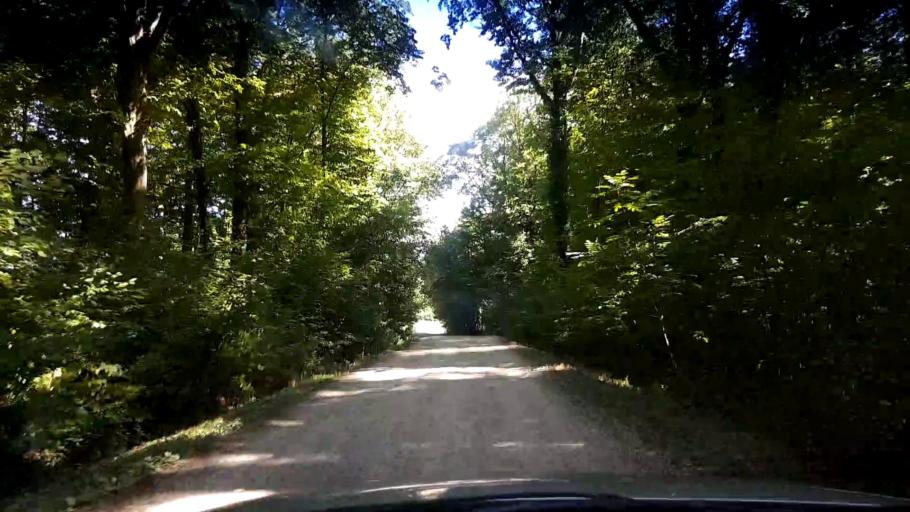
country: DE
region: Bavaria
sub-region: Upper Franconia
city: Schesslitz
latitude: 49.9554
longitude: 11.0346
